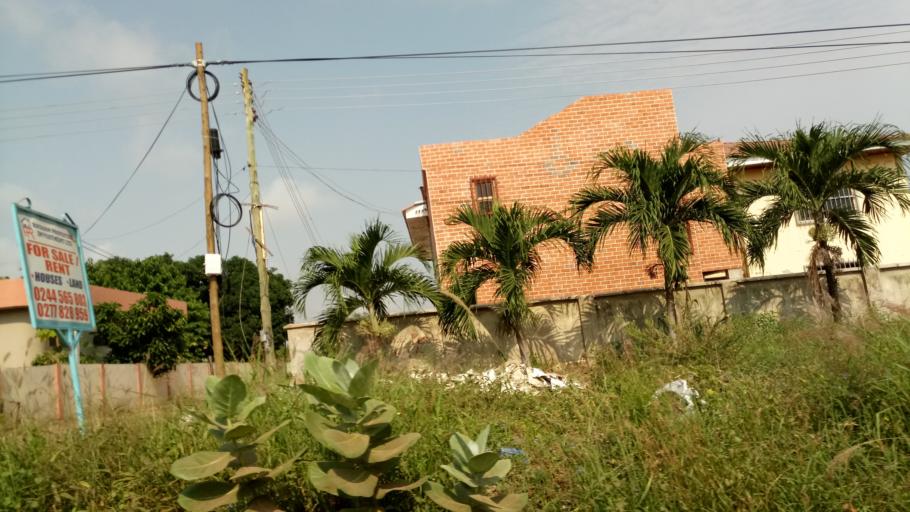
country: GH
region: Greater Accra
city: Medina Estates
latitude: 5.6743
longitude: -0.1909
